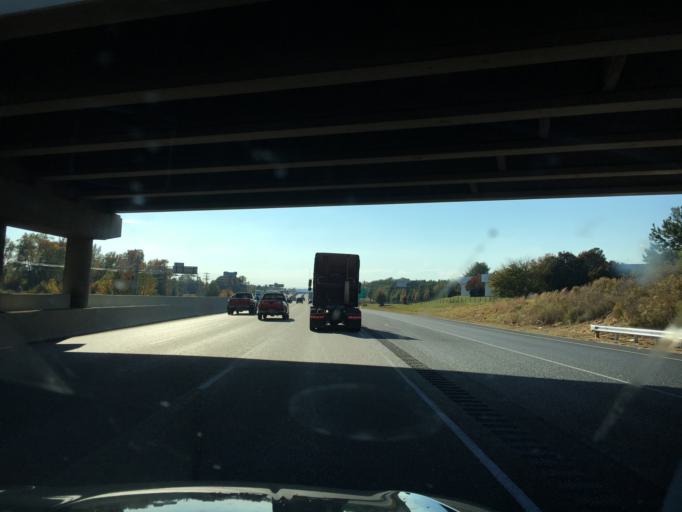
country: US
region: South Carolina
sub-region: Greenville County
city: Greer
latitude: 34.8850
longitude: -82.1950
